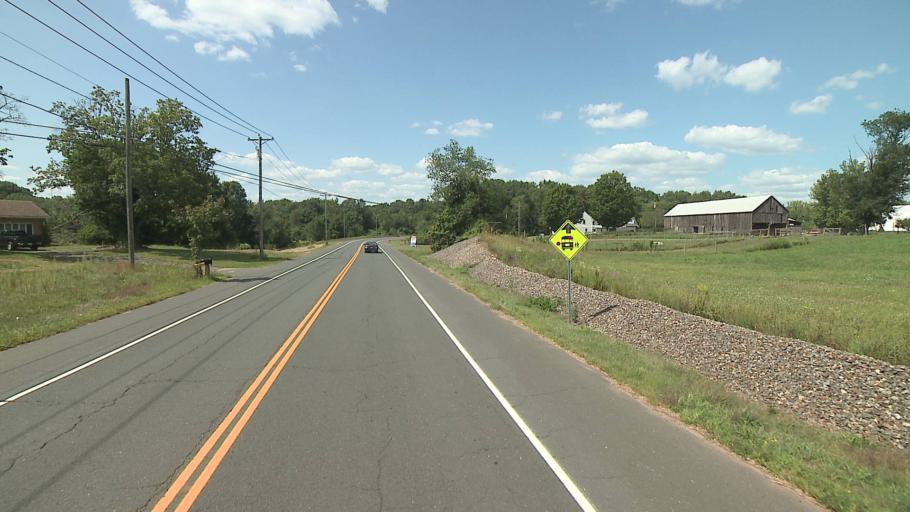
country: US
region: Connecticut
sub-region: Hartford County
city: Broad Brook
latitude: 41.9242
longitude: -72.5061
